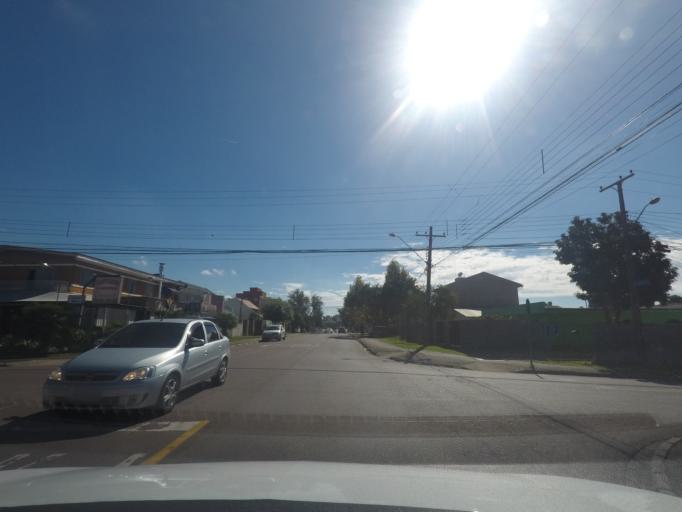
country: BR
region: Parana
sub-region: Sao Jose Dos Pinhais
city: Sao Jose dos Pinhais
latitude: -25.5035
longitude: -49.2734
